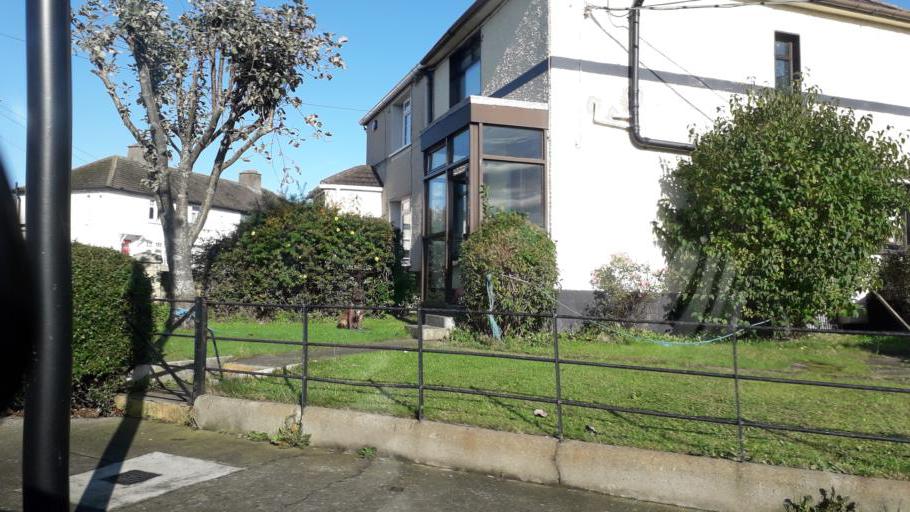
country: IE
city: Donnycarney
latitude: 53.3751
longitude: -6.2111
